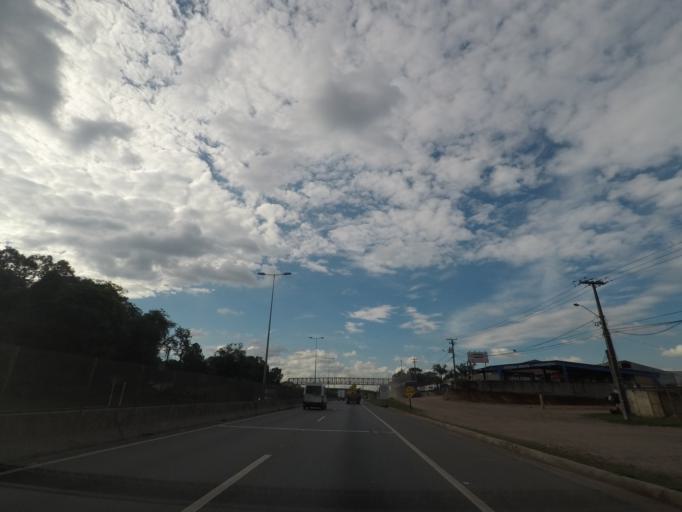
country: BR
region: Parana
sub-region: Araucaria
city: Araucaria
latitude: -25.5690
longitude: -49.3103
